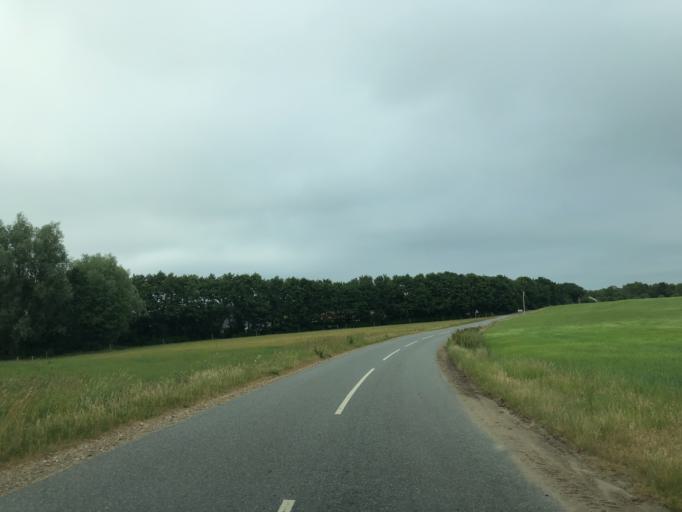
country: DK
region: Central Jutland
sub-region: Holstebro Kommune
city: Holstebro
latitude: 56.2545
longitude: 8.5602
